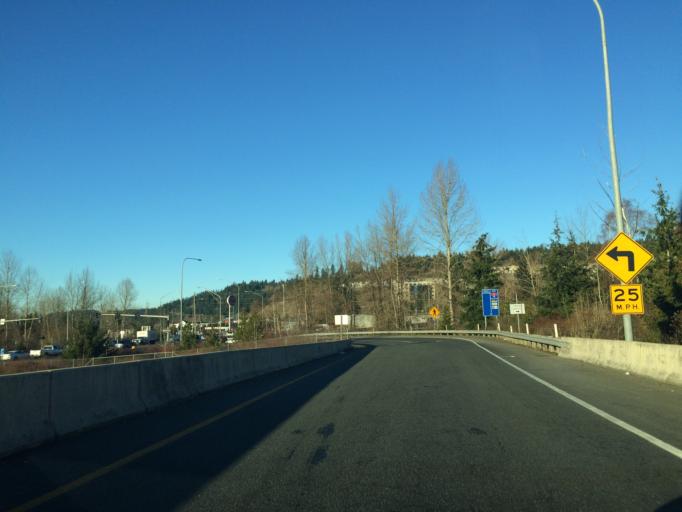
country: US
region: Washington
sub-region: King County
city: Issaquah
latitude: 47.5407
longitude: -122.0350
